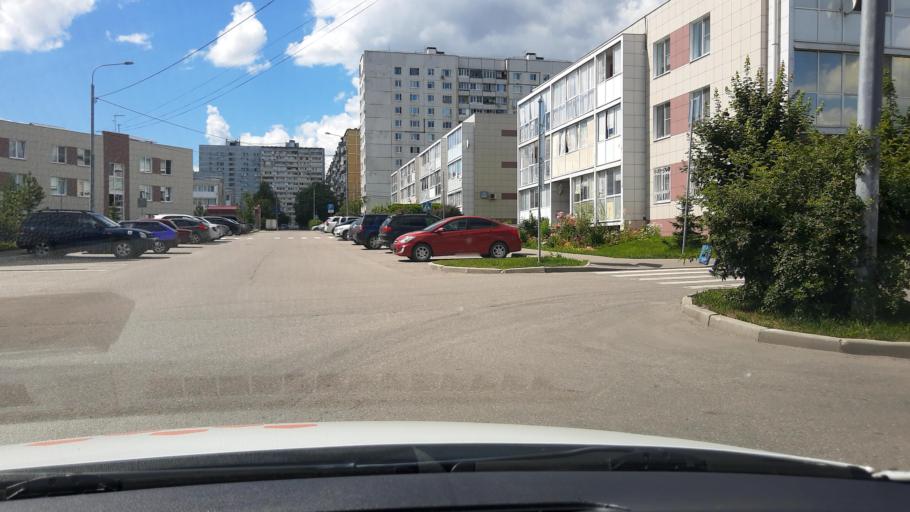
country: RU
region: Moskovskaya
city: Poselok Mar'ino
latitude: 55.5482
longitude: 37.3284
